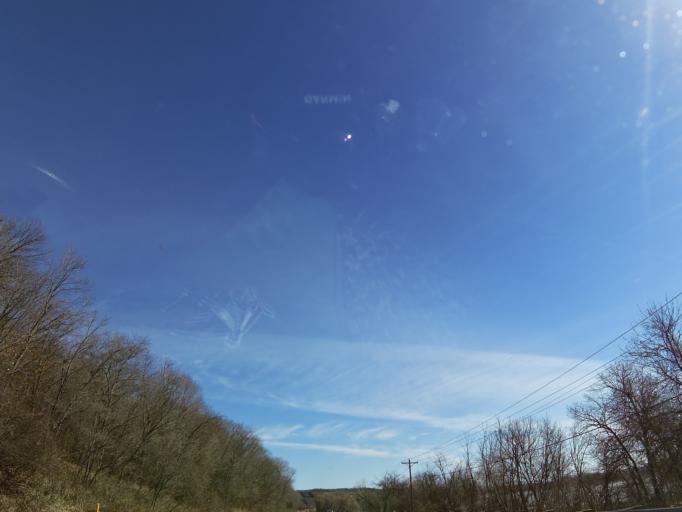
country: US
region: Minnesota
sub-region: Scott County
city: Shakopee
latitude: 44.8154
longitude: -93.5260
